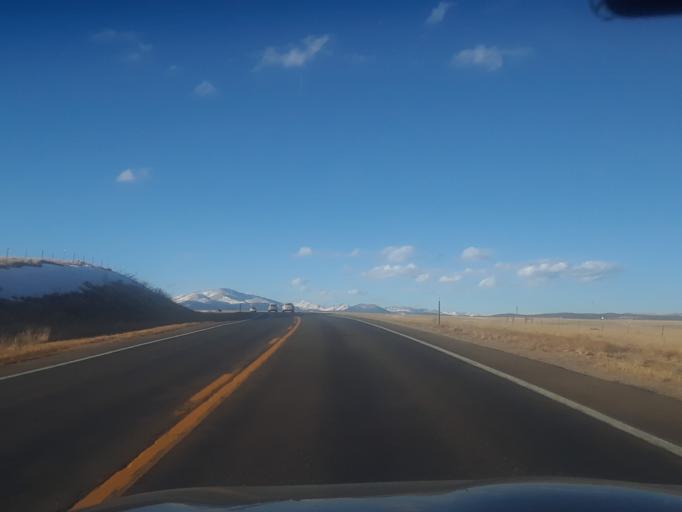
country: US
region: Colorado
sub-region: Park County
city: Fairplay
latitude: 39.0728
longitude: -105.9741
